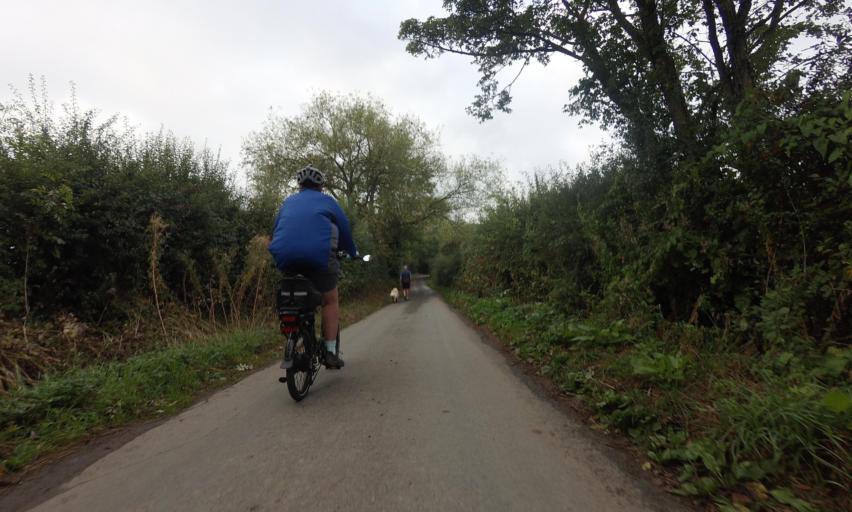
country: GB
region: England
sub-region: Gloucestershire
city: Gotherington
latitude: 51.9859
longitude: -2.0253
